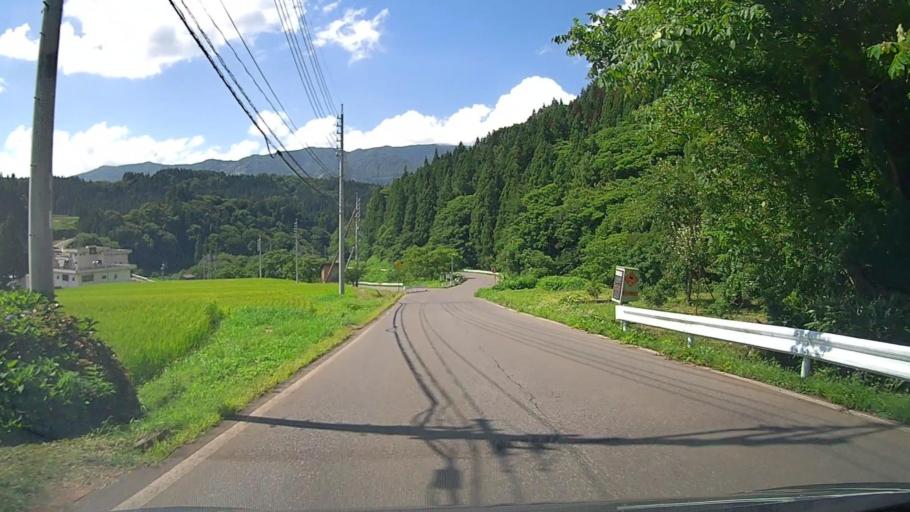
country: JP
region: Nagano
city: Iiyama
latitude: 36.9236
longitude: 138.4293
